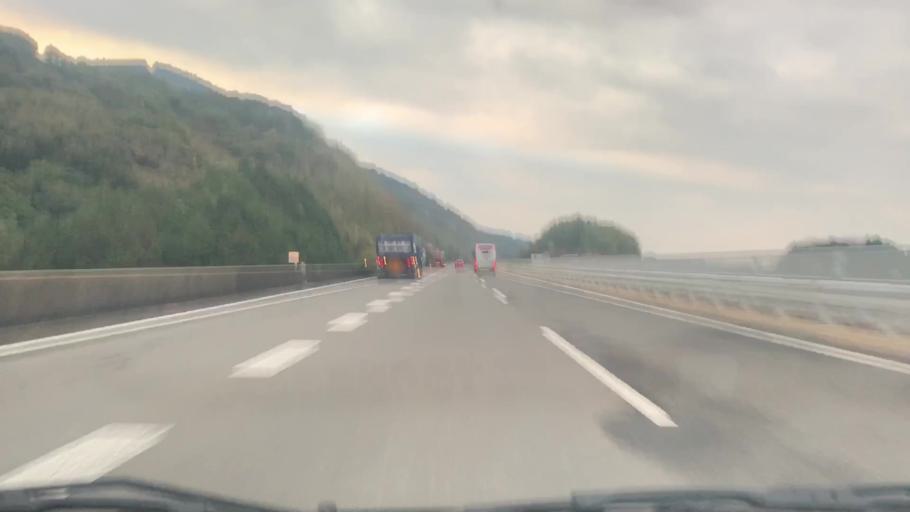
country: JP
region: Nagasaki
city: Omura
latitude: 32.9913
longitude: 129.9561
